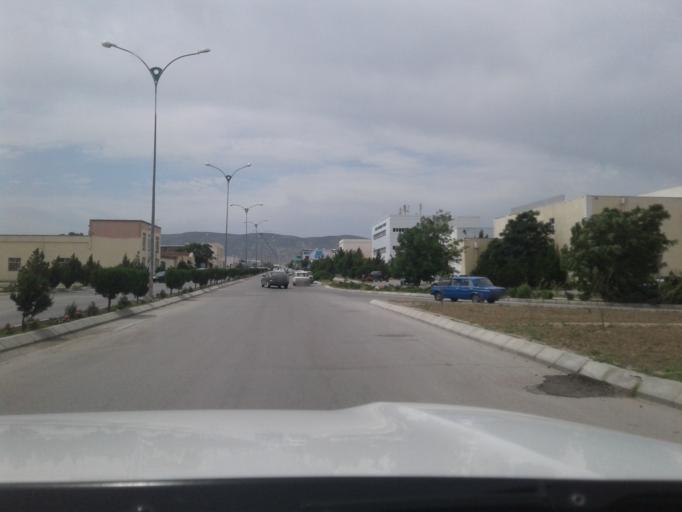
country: TM
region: Balkan
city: Serdar
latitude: 38.9772
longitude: 56.2777
